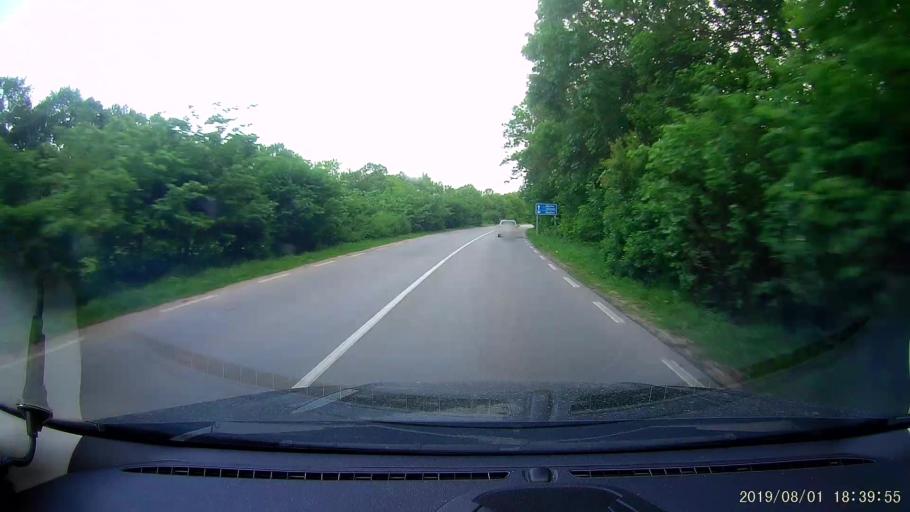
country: BG
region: Shumen
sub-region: Obshtina Khitrino
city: Gara Khitrino
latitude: 43.3760
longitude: 26.9195
